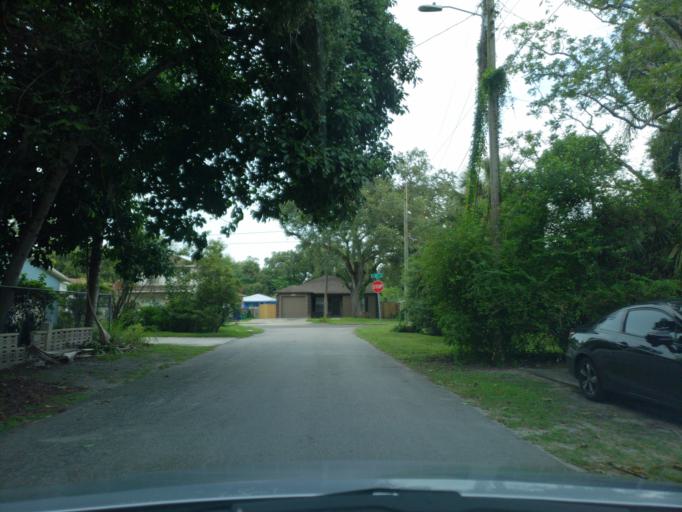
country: US
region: Florida
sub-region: Hillsborough County
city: Tampa
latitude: 27.9709
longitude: -82.4327
